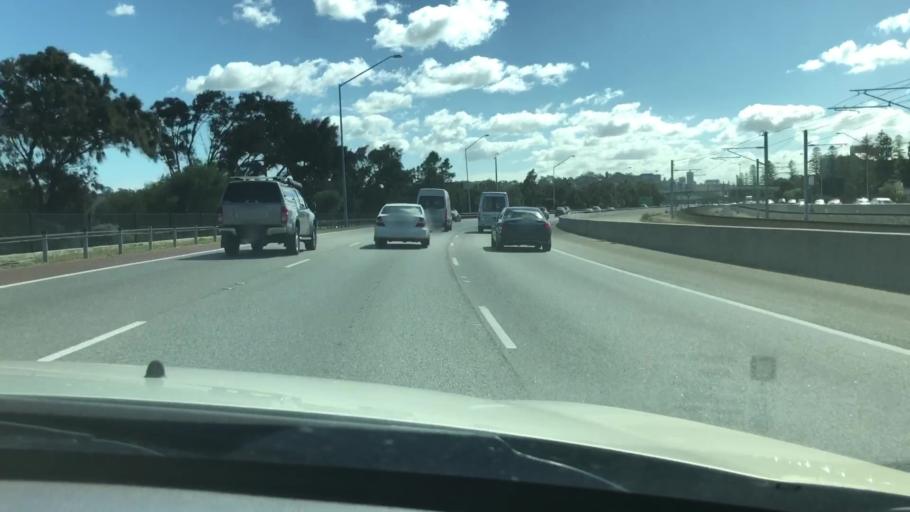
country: AU
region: Western Australia
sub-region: South Perth
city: South Perth
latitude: -31.9800
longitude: 115.8503
